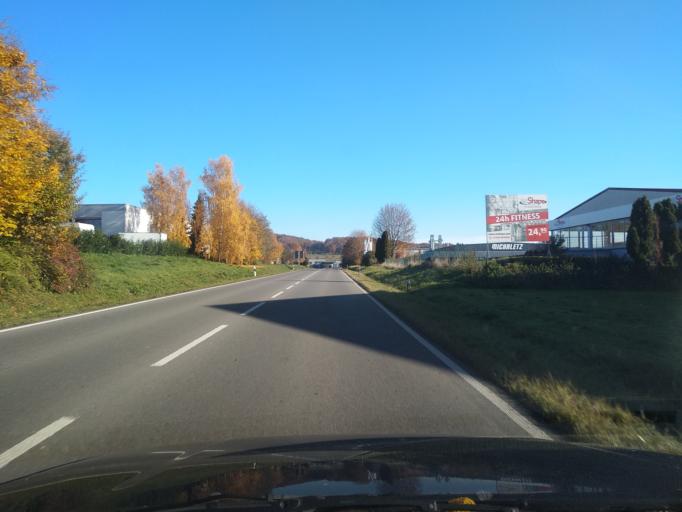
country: DE
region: Baden-Wuerttemberg
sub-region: Karlsruhe Region
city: Althengstett
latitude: 48.7246
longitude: 8.7822
